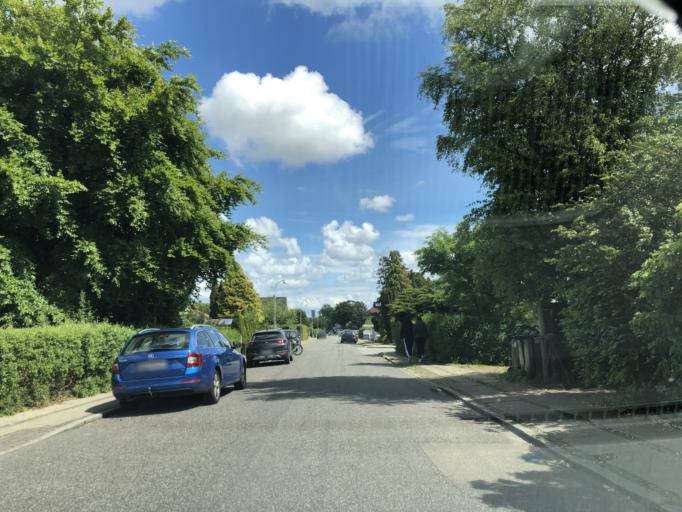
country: DK
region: Capital Region
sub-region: Hvidovre Kommune
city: Hvidovre
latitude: 55.6636
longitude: 12.4638
